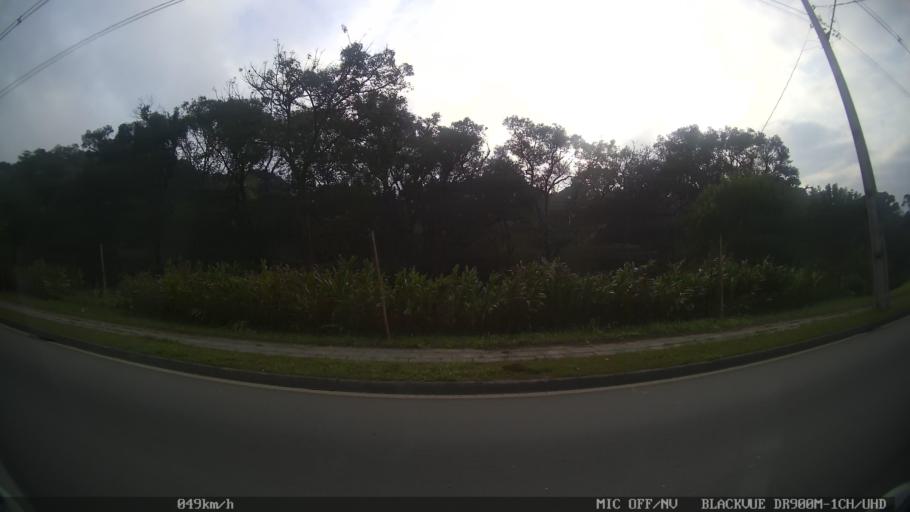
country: BR
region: Parana
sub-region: Curitiba
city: Curitiba
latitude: -25.3860
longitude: -49.3073
